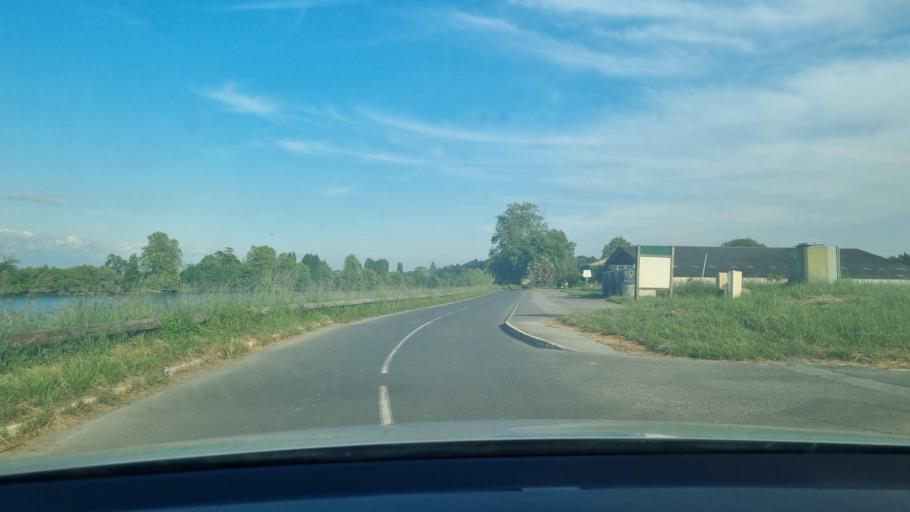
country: FR
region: Aquitaine
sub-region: Departement des Landes
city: Peyrehorade
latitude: 43.5439
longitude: -1.1682
